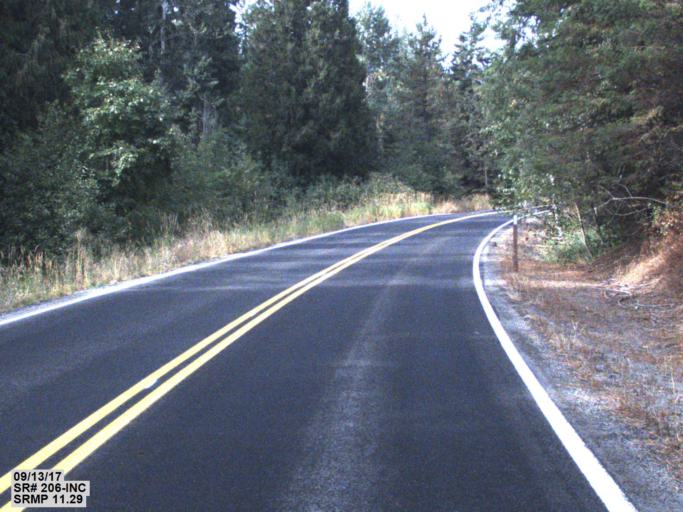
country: US
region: Washington
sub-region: Spokane County
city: Trentwood
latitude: 47.8404
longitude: -117.1725
